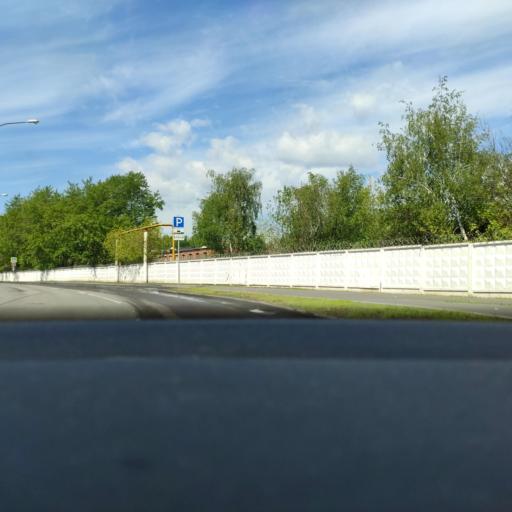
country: RU
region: Moscow
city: Altuf'yevskiy
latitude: 55.8831
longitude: 37.5820
